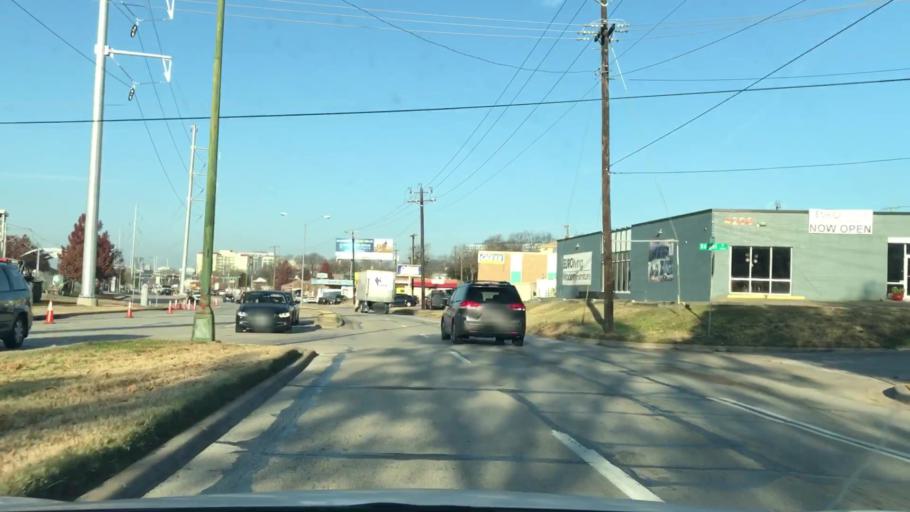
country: US
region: Texas
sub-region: Dallas County
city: Dallas
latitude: 32.8043
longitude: -96.8210
